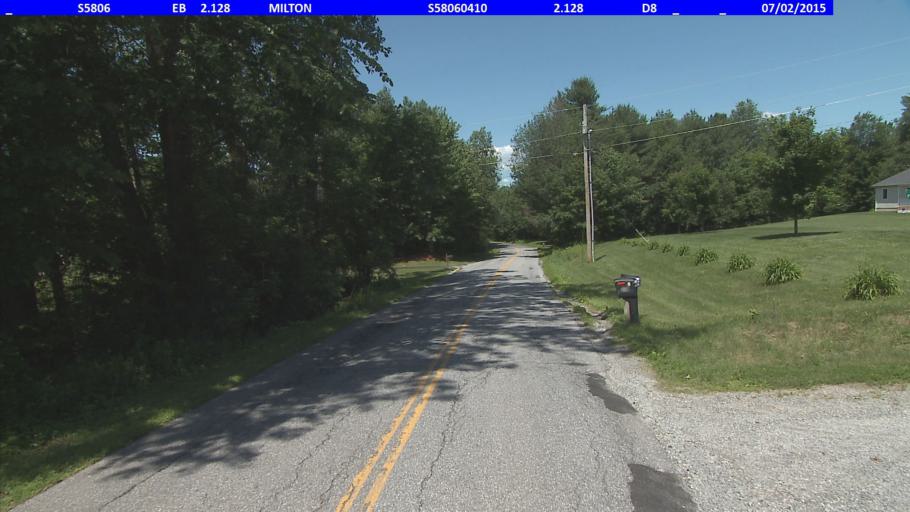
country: US
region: Vermont
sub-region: Chittenden County
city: Milton
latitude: 44.6629
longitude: -73.1516
